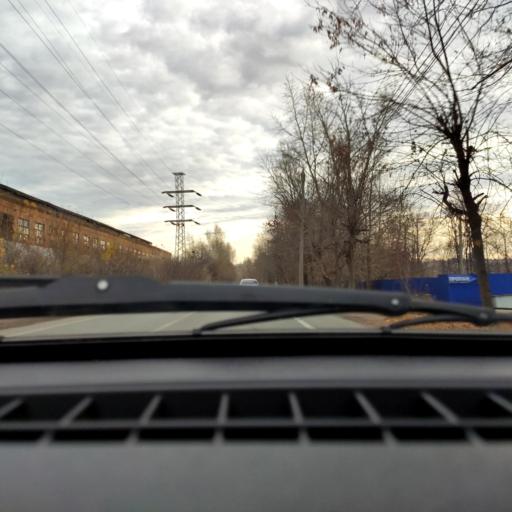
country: RU
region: Bashkortostan
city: Ufa
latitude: 54.8406
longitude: 56.0756
